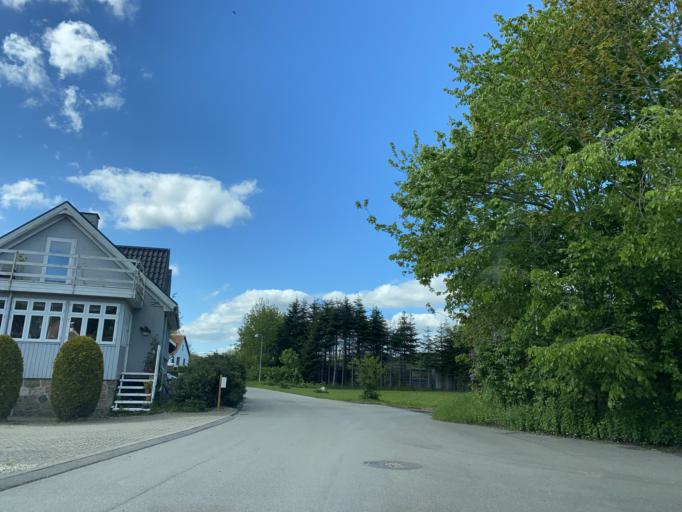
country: DK
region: Central Jutland
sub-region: Skanderborg Kommune
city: Galten
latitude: 56.1684
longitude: 9.8488
